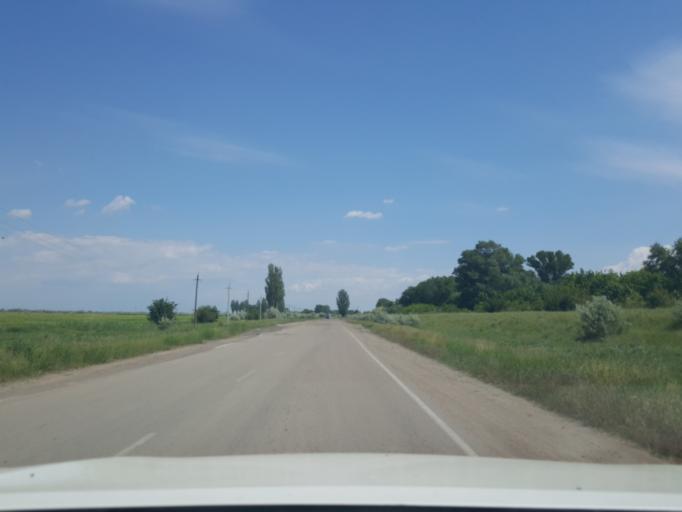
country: RO
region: Tulcea
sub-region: Oras Isaccea
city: Isaccea
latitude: 45.3016
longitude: 28.4240
